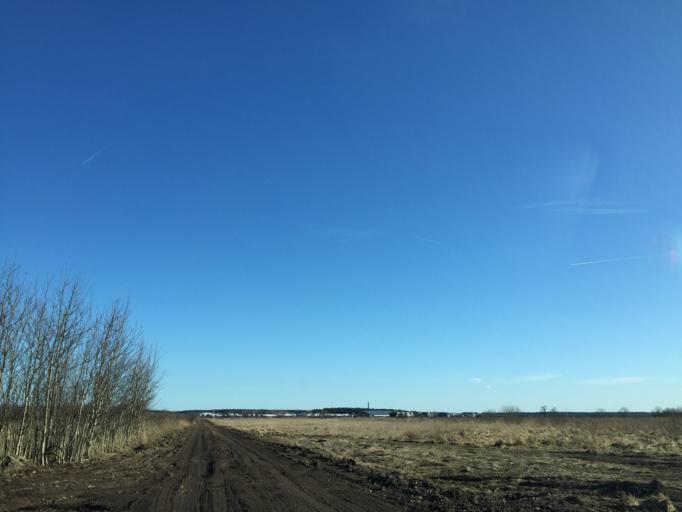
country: LV
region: Babite
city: Pinki
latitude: 56.9665
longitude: 23.8851
